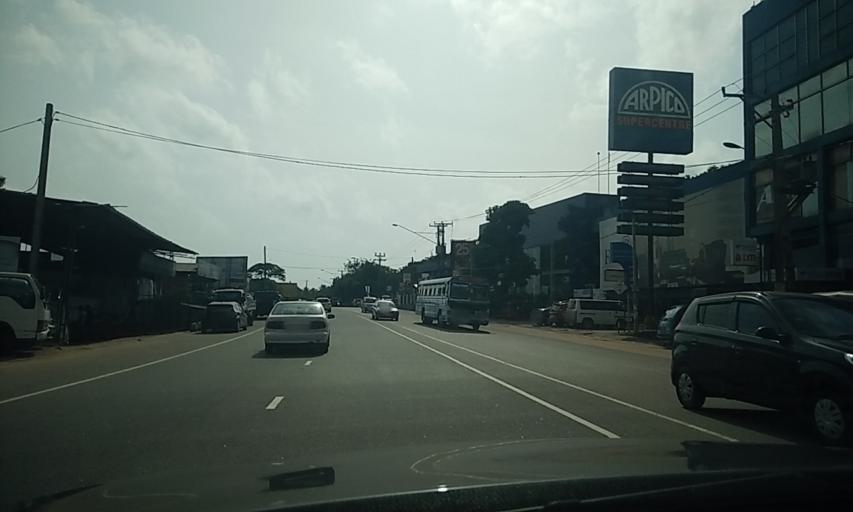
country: LK
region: Western
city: Maharagama
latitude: 6.8523
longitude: 79.9184
